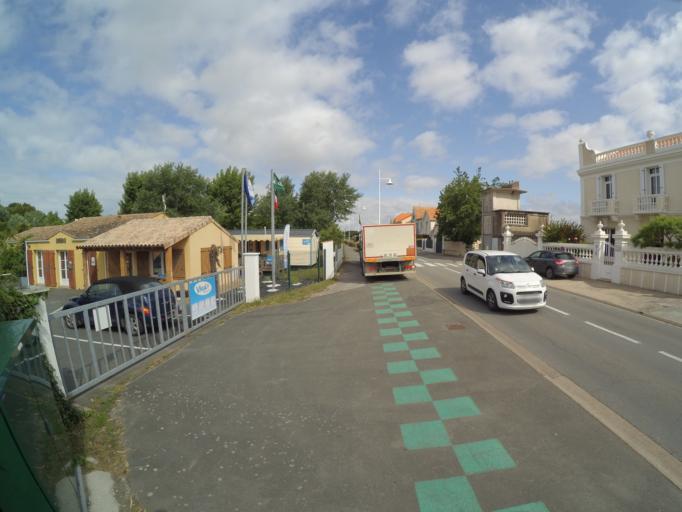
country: FR
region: Poitou-Charentes
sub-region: Departement de la Charente-Maritime
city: Chatelaillon-Plage
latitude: 46.0844
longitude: -1.0933
